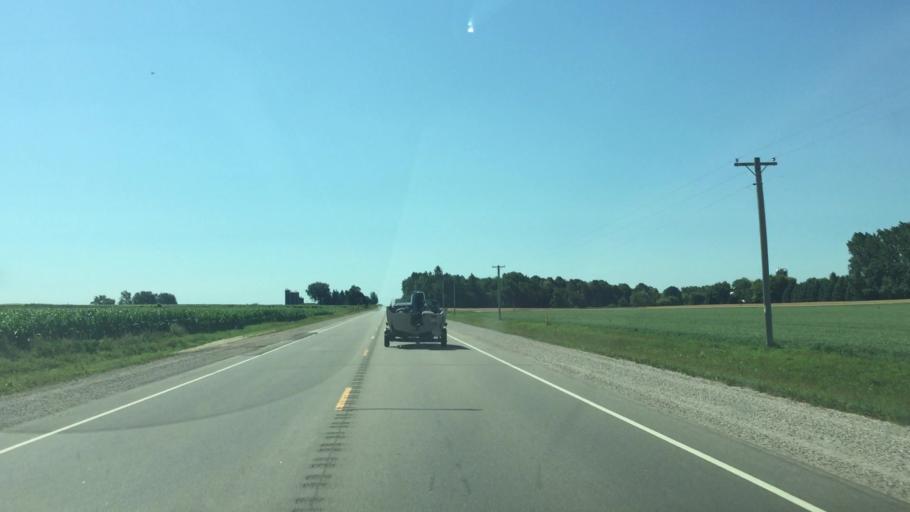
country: US
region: Wisconsin
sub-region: Calumet County
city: Chilton
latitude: 43.9981
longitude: -88.1310
